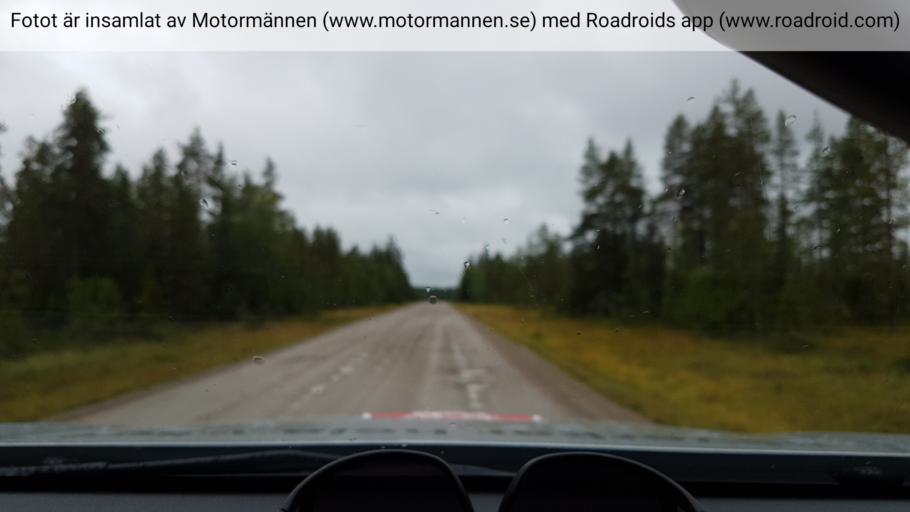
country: SE
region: Vaesterbotten
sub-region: Lycksele Kommun
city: Soderfors
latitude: 64.7637
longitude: 17.6588
